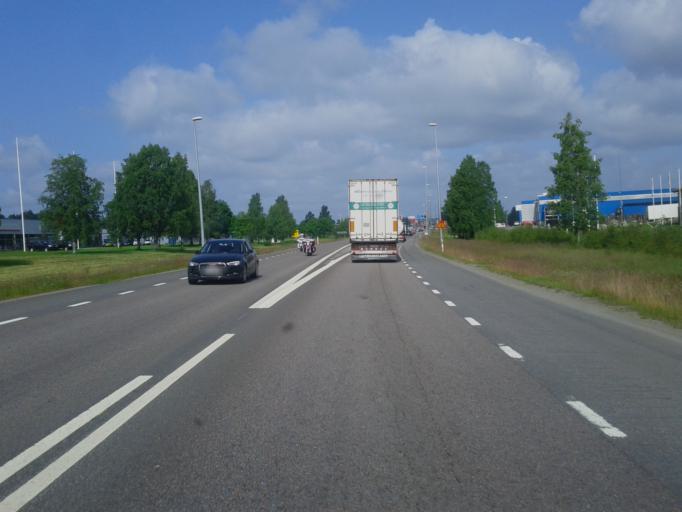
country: SE
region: Vaesterbotten
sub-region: Skelleftea Kommun
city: Skelleftea
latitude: 64.7342
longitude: 20.9694
